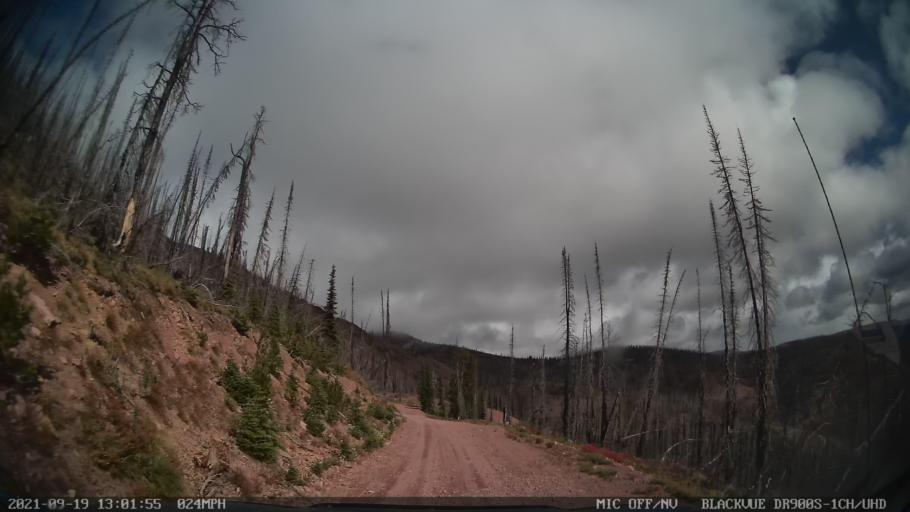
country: US
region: Montana
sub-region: Missoula County
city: Seeley Lake
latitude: 47.1878
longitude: -113.3542
